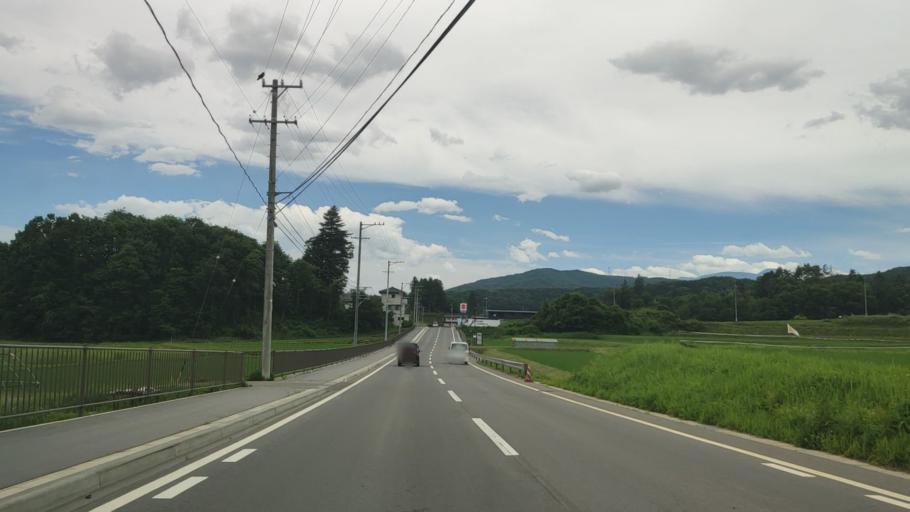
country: JP
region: Nagano
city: Kamimaruko
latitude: 36.2804
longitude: 138.2913
